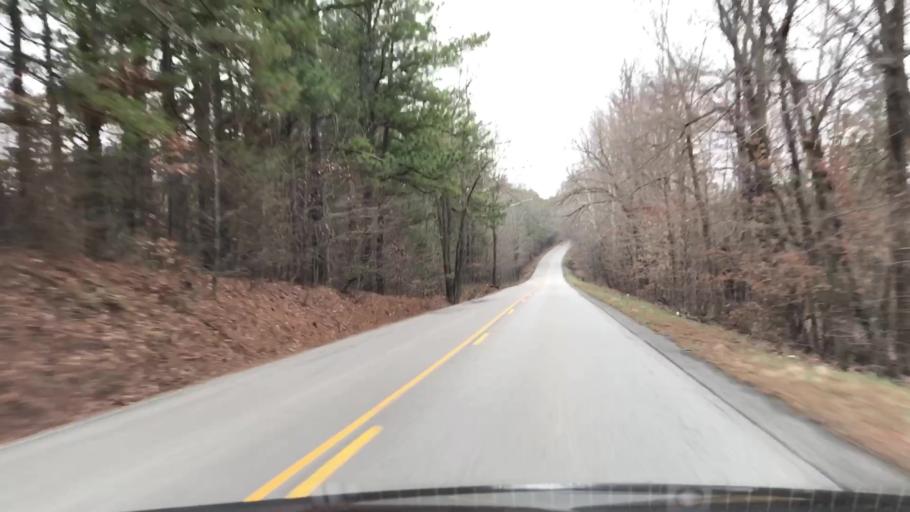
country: US
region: Kentucky
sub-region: Muhlenberg County
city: Morehead
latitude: 37.2842
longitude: -87.2099
